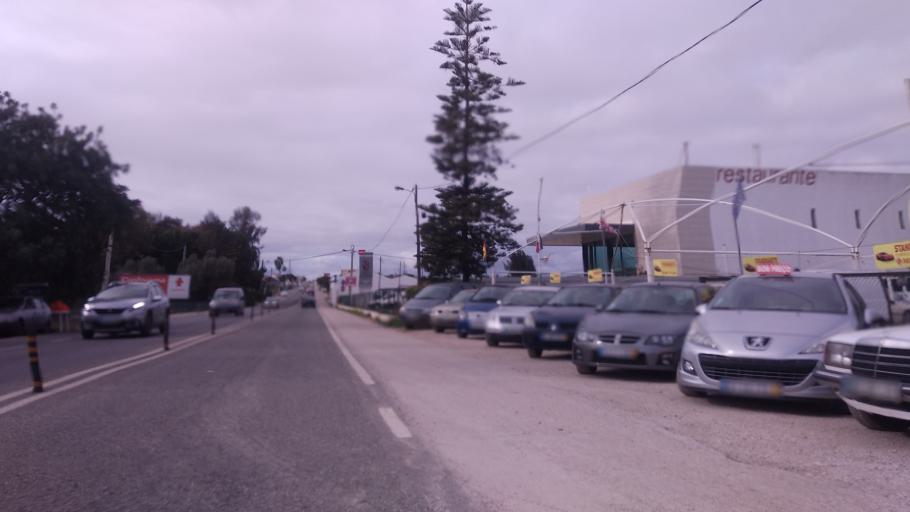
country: PT
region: Faro
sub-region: Albufeira
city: Ferreiras
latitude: 37.1289
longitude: -8.2659
